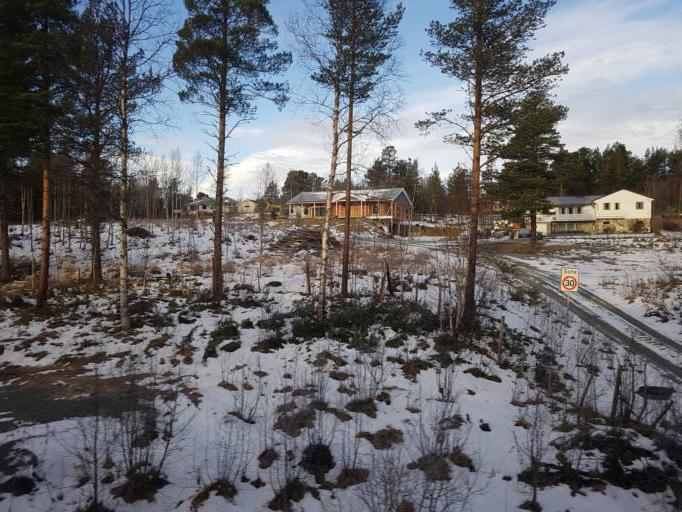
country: NO
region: Sor-Trondelag
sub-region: Oppdal
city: Oppdal
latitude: 62.6573
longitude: 9.8796
